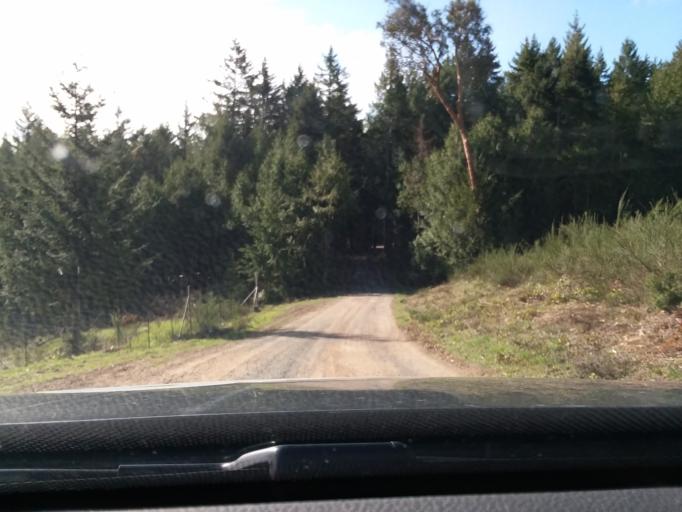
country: CA
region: British Columbia
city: North Saanich
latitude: 48.8757
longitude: -123.3301
